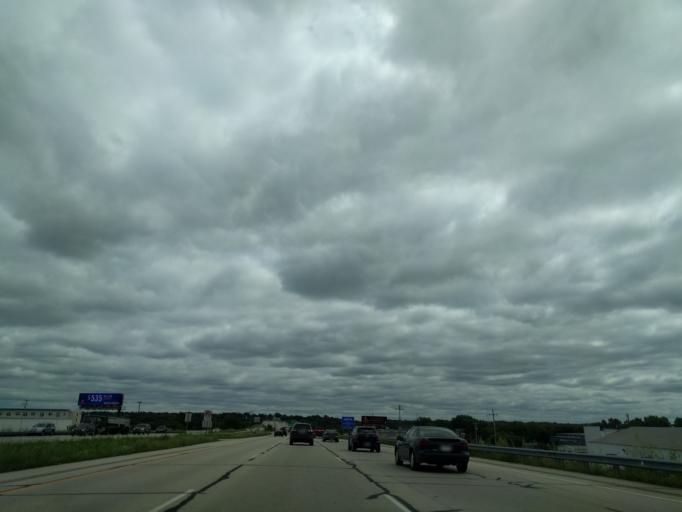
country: US
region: Wisconsin
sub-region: Brown County
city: Ashwaubenon
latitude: 44.4776
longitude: -88.0578
